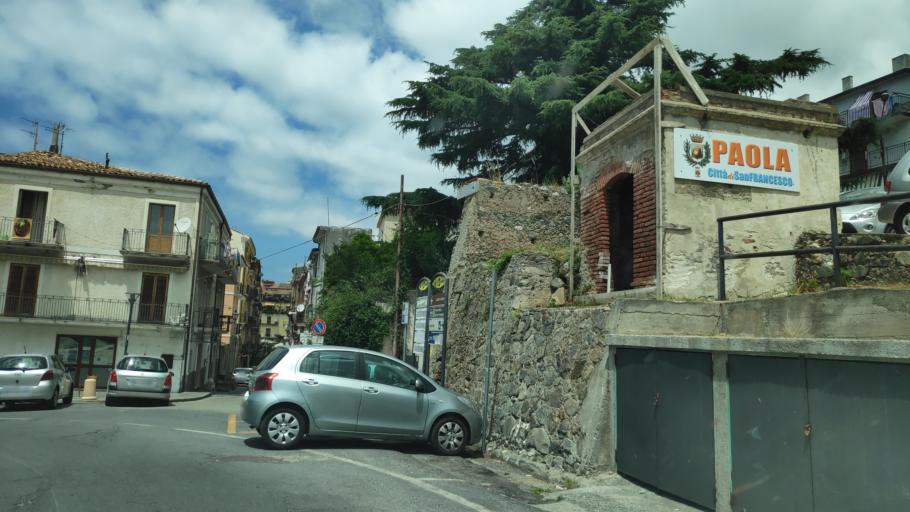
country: IT
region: Calabria
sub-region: Provincia di Cosenza
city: Paola
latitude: 39.3575
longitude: 16.0425
